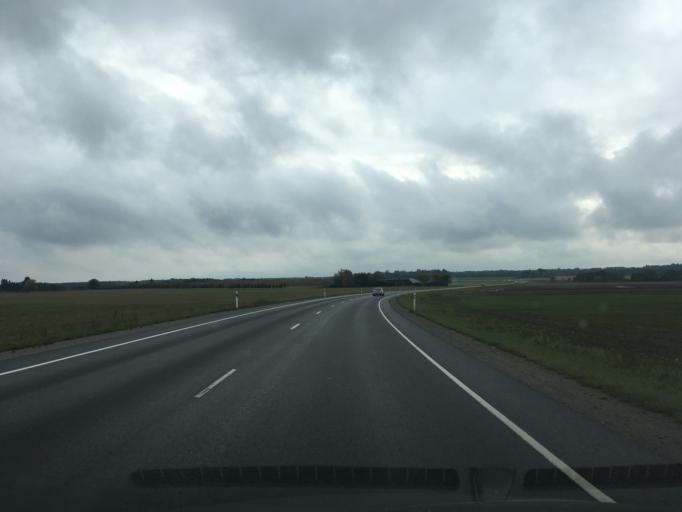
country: EE
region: Harju
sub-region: Saue linn
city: Saue
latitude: 59.3532
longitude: 24.4923
